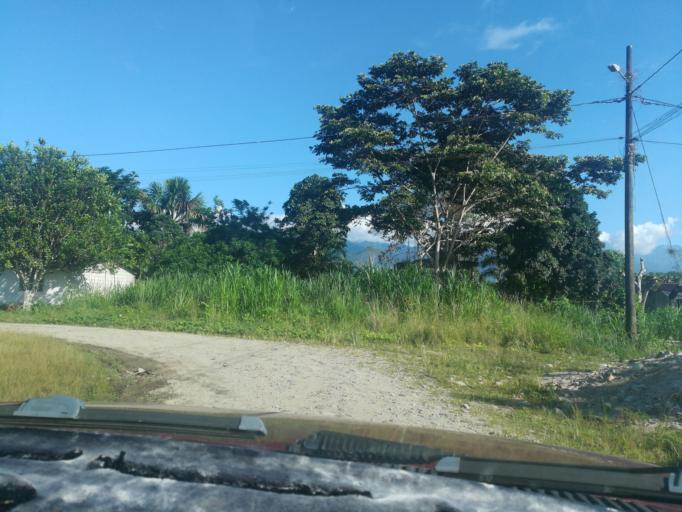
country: EC
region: Napo
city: Tena
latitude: -0.9916
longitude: -77.8332
